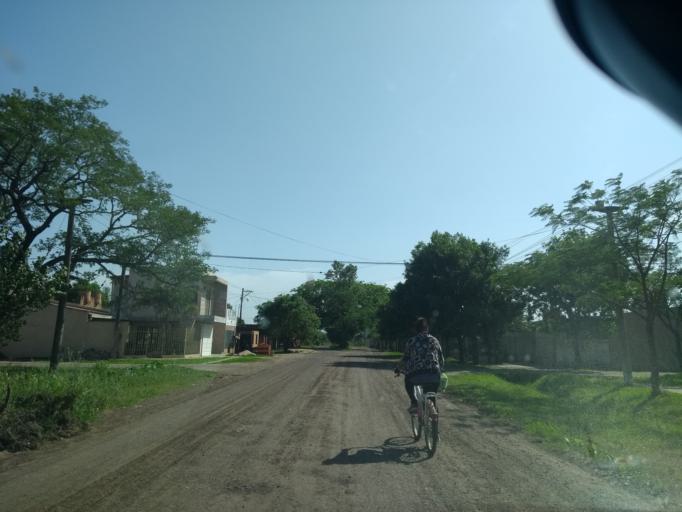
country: AR
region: Chaco
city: Fontana
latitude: -27.4161
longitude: -59.0399
